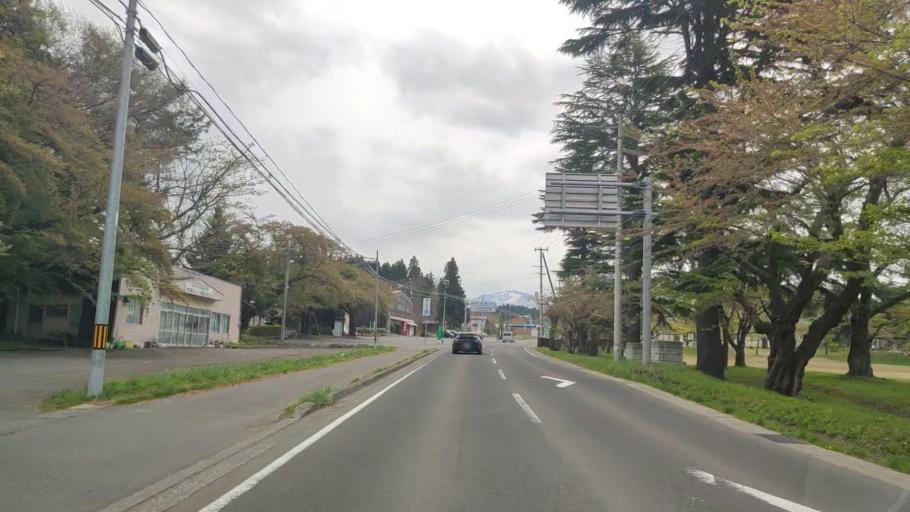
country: JP
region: Aomori
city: Aomori Shi
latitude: 40.7860
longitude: 140.7893
